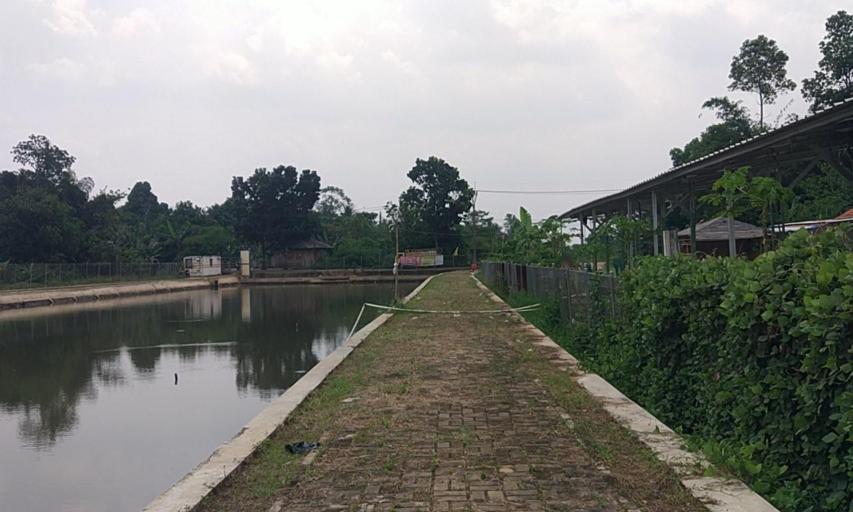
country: ID
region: West Java
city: Parung
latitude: -6.4742
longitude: 106.7763
